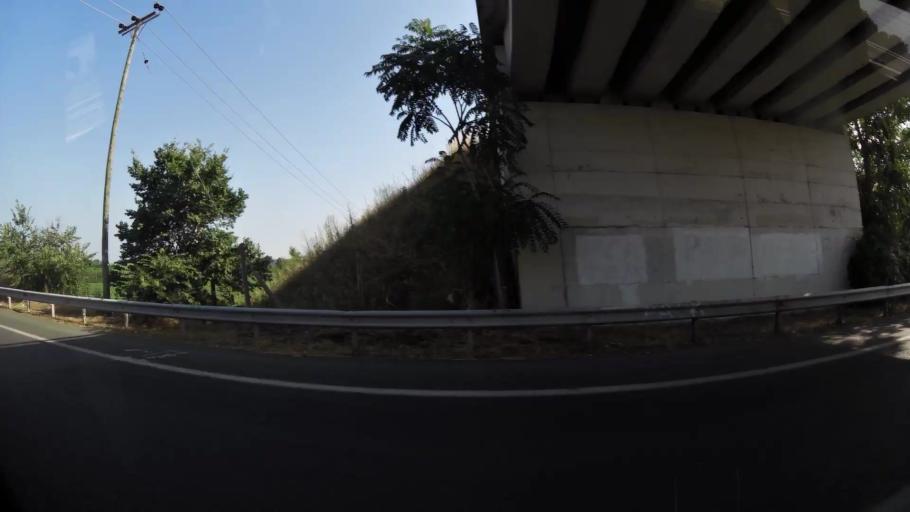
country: GR
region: Central Macedonia
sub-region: Nomos Imathias
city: Agkathia
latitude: 40.5873
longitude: 22.4724
